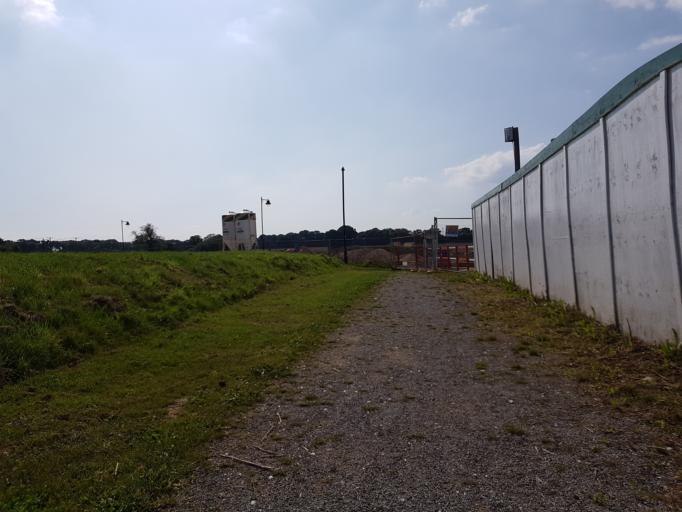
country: GB
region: England
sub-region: Hampshire
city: Waterlooville
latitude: 50.8789
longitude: -1.0417
